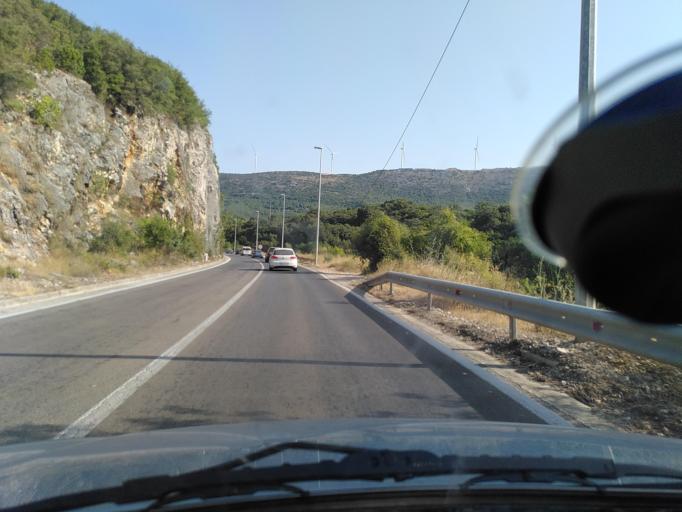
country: ME
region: Ulcinj
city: Ulcinj
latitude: 41.9621
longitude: 19.1915
